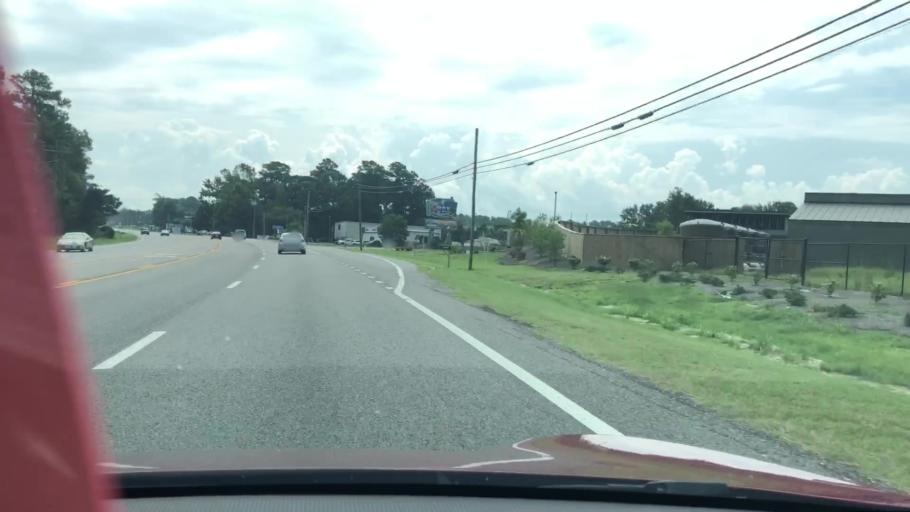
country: US
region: North Carolina
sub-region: Dare County
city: Southern Shores
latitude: 36.1116
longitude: -75.8263
